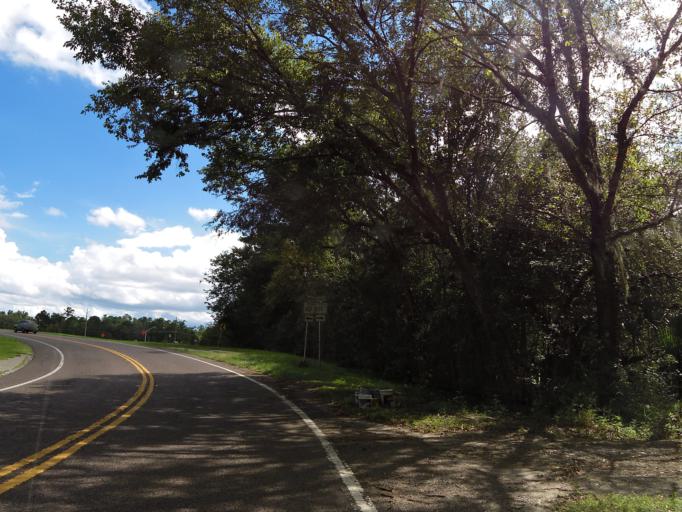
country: US
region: Florida
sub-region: Putnam County
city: East Palatka
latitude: 29.7428
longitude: -81.4755
